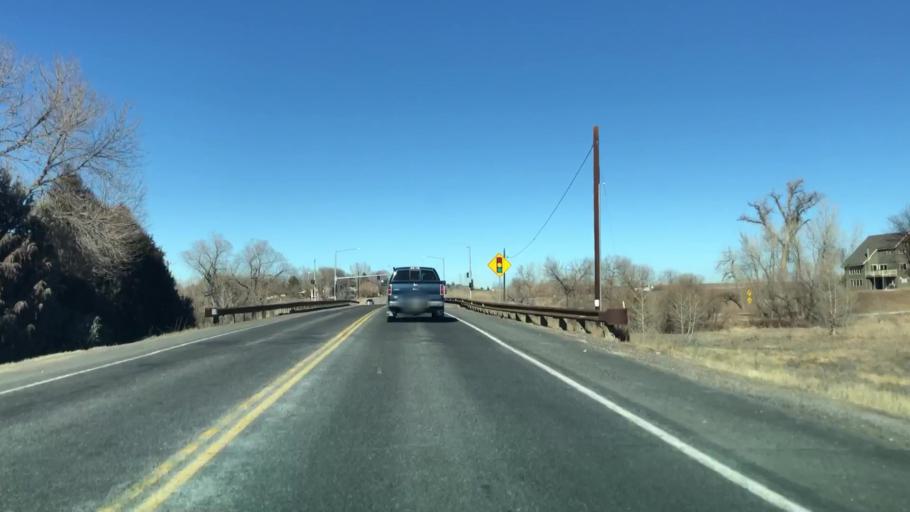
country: US
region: Colorado
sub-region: Weld County
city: Windsor
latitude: 40.5213
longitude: -104.9820
